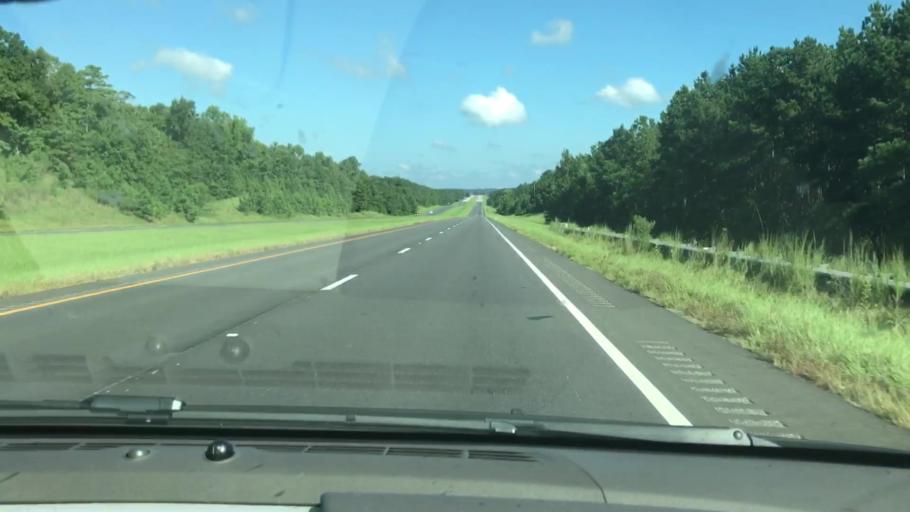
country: US
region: Alabama
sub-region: Barbour County
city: Eufaula
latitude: 32.0499
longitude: -85.1329
